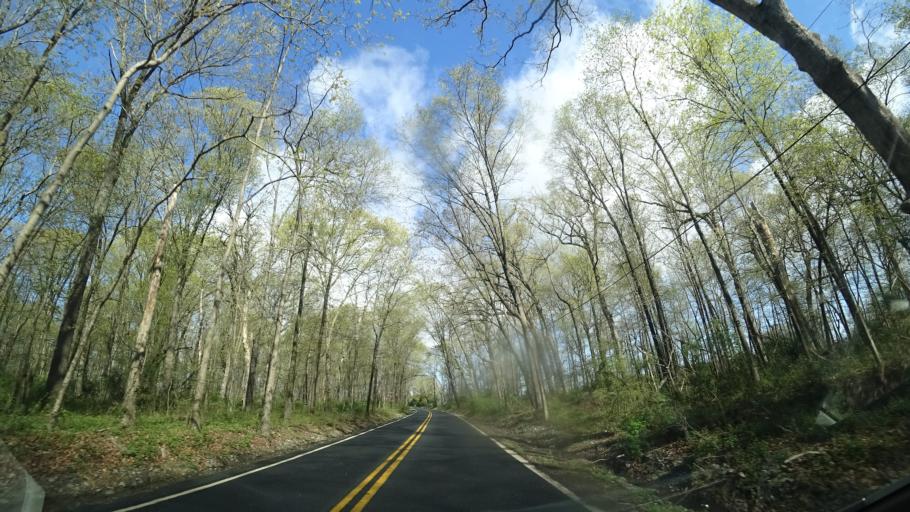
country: US
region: Virginia
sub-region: Loudoun County
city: Lowes Island
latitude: 39.0827
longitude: -77.3543
